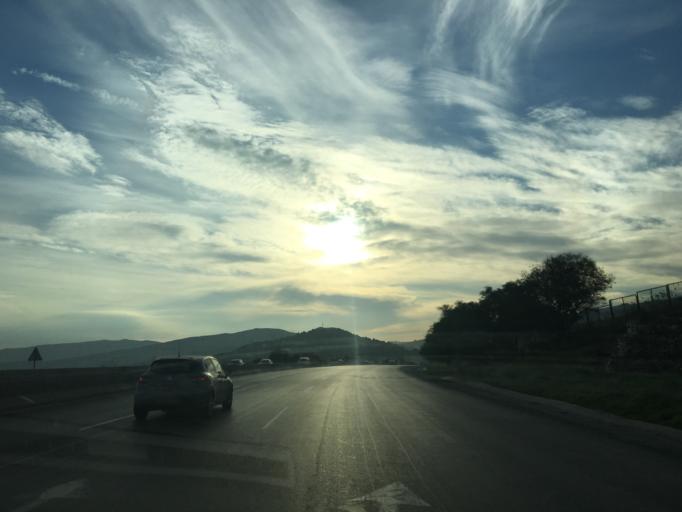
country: DZ
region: Bouira
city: Draa el Mizan
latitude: 36.4713
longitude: 3.7626
